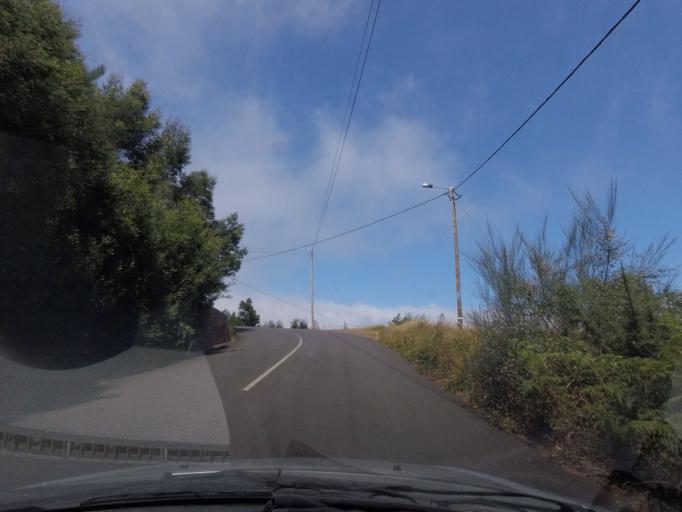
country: PT
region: Madeira
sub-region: Santa Cruz
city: Camacha
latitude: 32.6863
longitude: -16.8269
